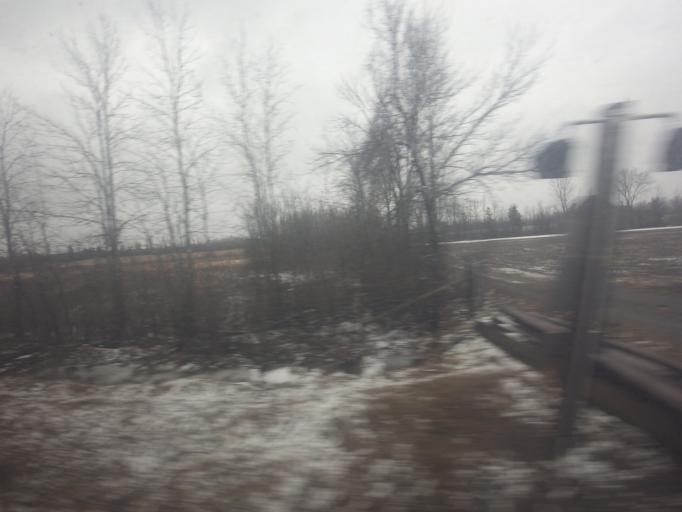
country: CA
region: Ontario
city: Deseronto
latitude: 44.2243
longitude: -77.1240
